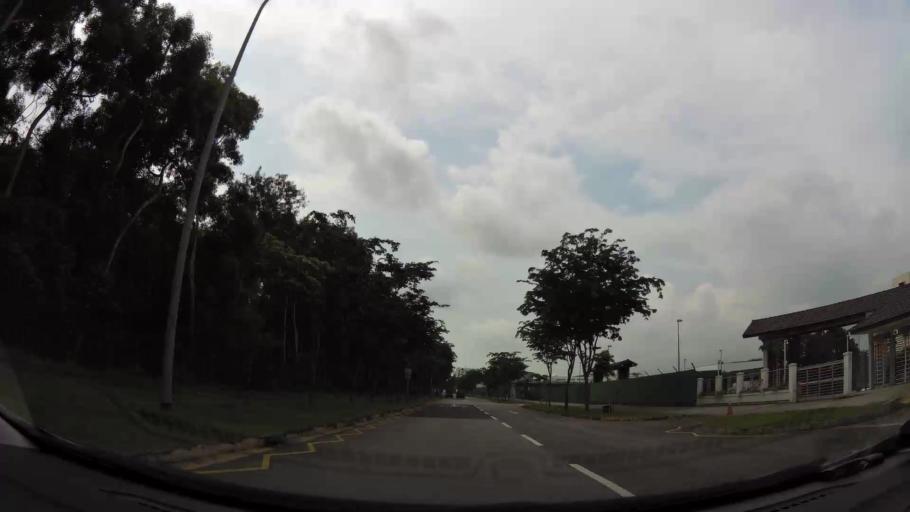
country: SG
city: Singapore
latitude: 1.3571
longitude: 103.9756
